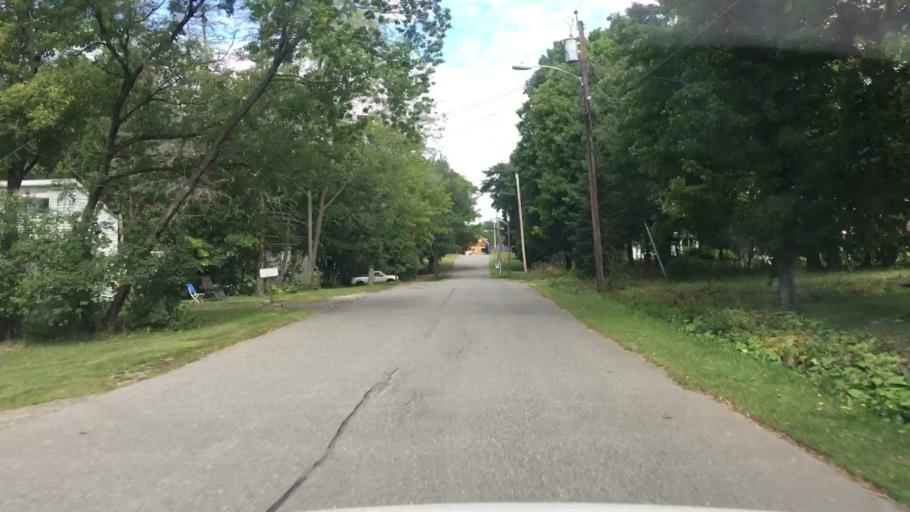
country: US
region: Maine
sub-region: Piscataquis County
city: Dover-Foxcroft
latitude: 45.1888
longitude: -69.2226
